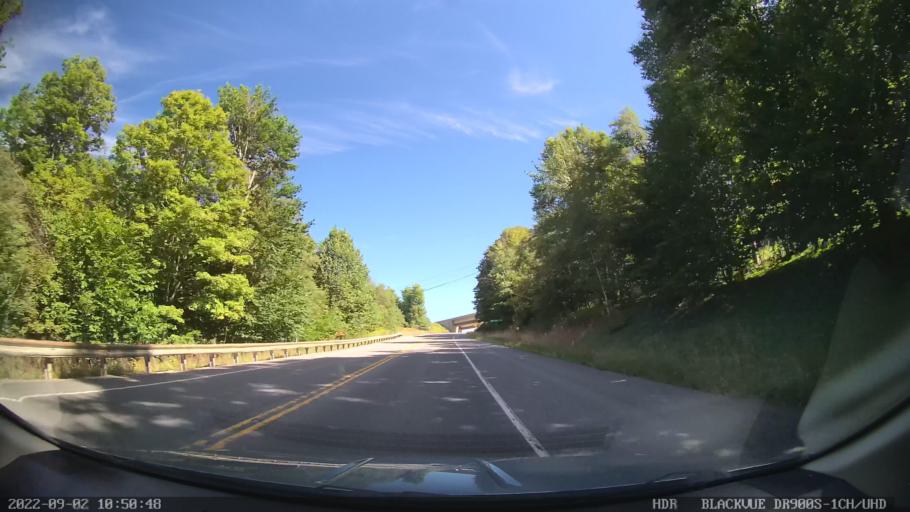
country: US
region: Pennsylvania
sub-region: Tioga County
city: Blossburg
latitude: 41.6186
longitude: -77.1193
